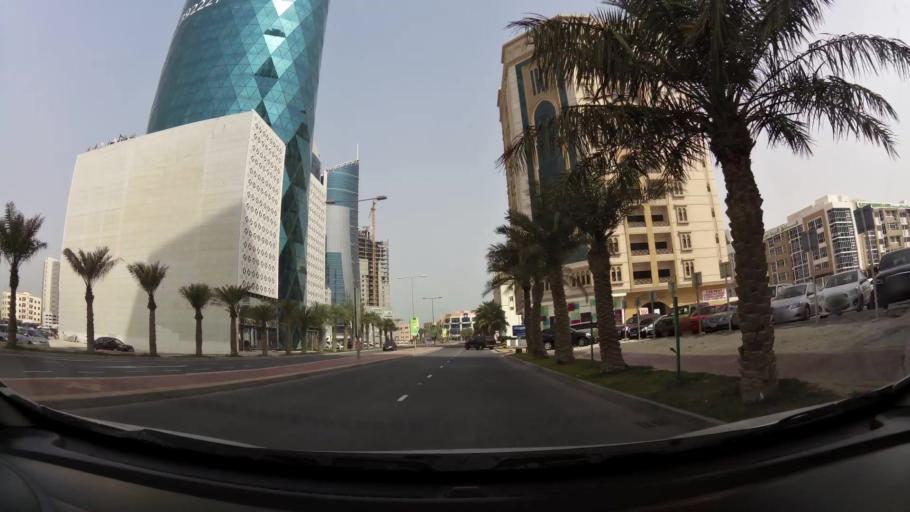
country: BH
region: Manama
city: Jidd Hafs
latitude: 26.2385
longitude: 50.5372
